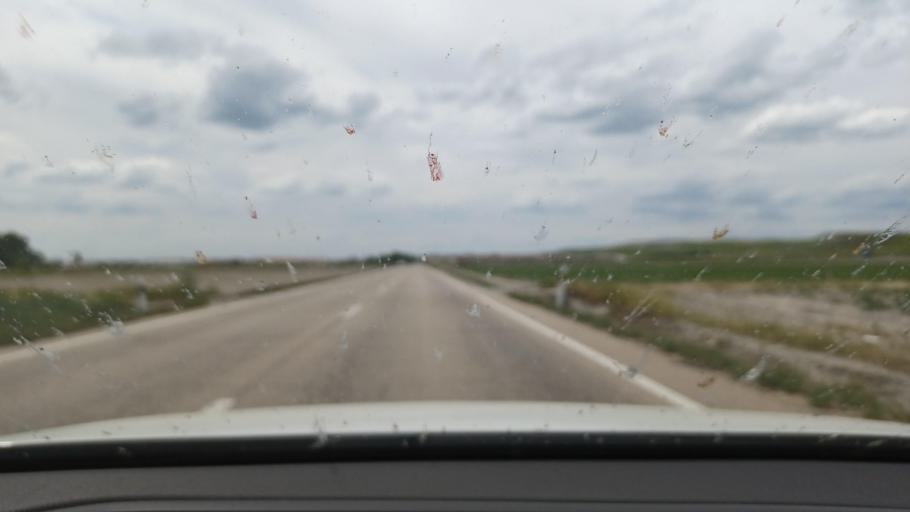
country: ES
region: Castille and Leon
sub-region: Provincia de Segovia
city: Frumales
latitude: 41.3832
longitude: -4.2306
